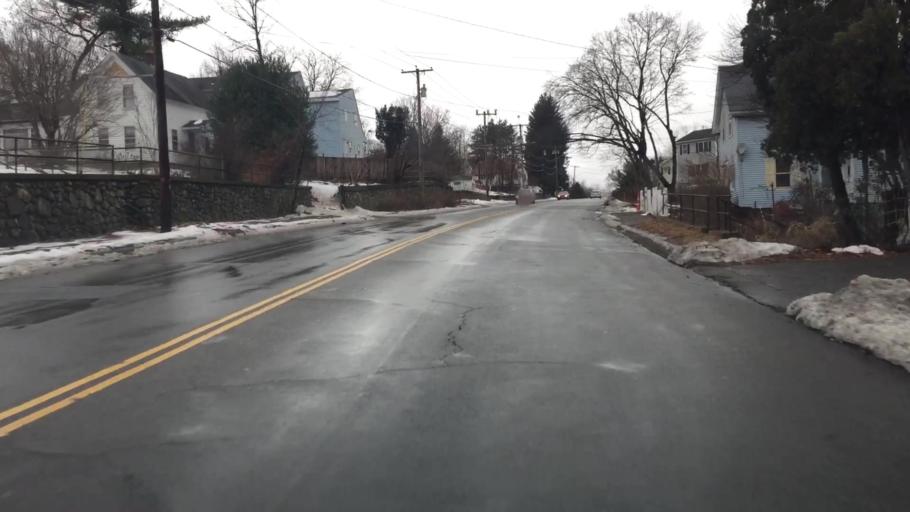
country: US
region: Massachusetts
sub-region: Worcester County
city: West Boylston
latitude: 42.3206
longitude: -71.7855
